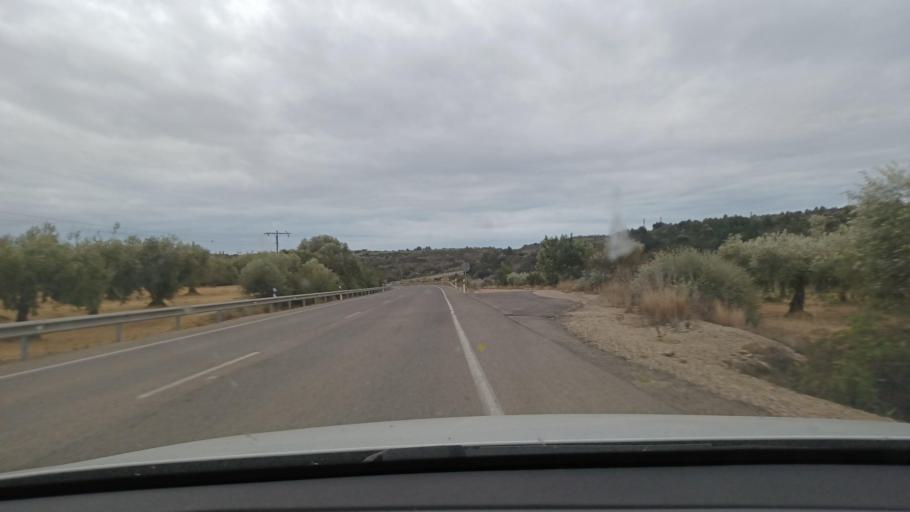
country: ES
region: Valencia
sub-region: Provincia de Castello
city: Traiguera
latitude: 40.5219
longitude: 0.3064
